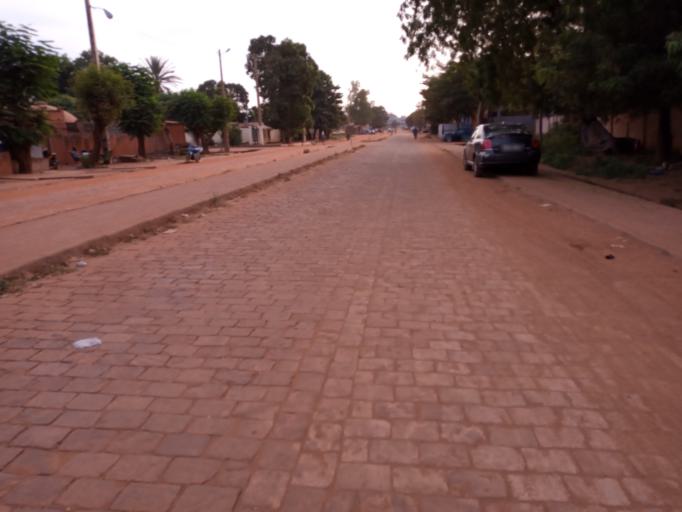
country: ML
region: Bamako
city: Bamako
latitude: 12.5945
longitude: -7.9572
